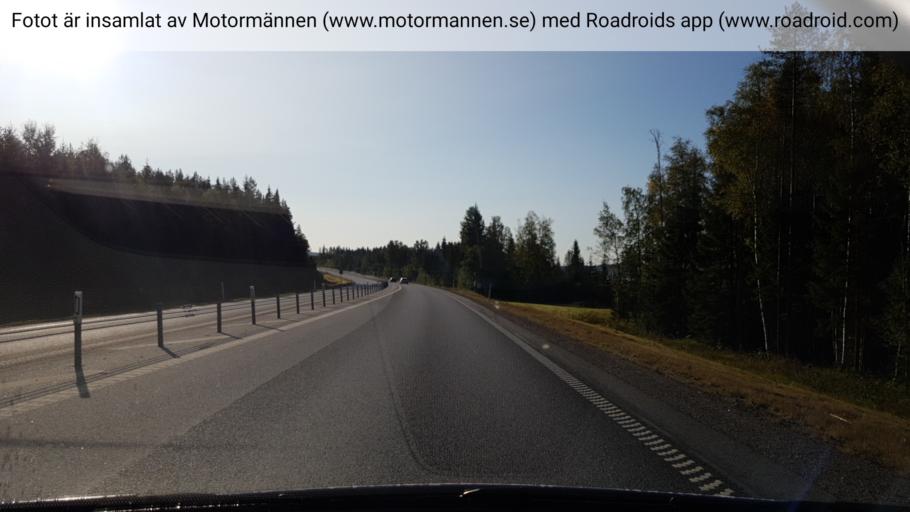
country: SE
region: Vaesterbotten
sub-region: Vannas Kommun
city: Vannasby
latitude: 63.9031
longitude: 19.8954
